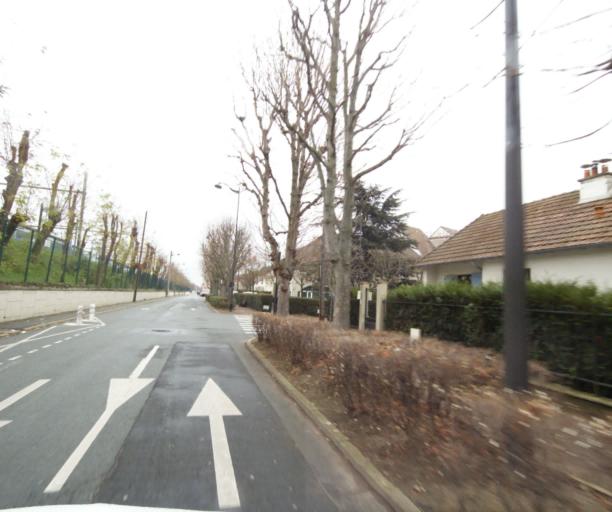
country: FR
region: Ile-de-France
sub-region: Departement des Yvelines
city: Chatou
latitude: 48.8881
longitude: 2.1747
